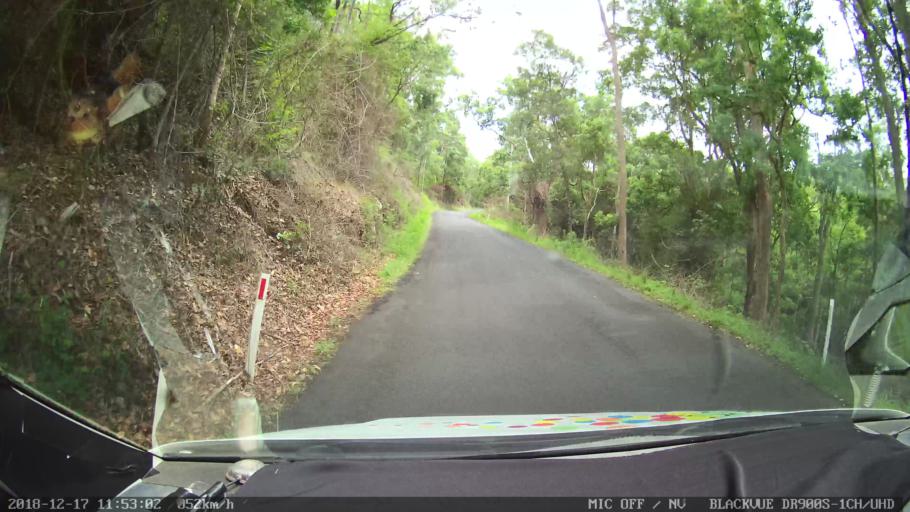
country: AU
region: New South Wales
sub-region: Kyogle
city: Kyogle
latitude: -28.5772
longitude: 152.5875
